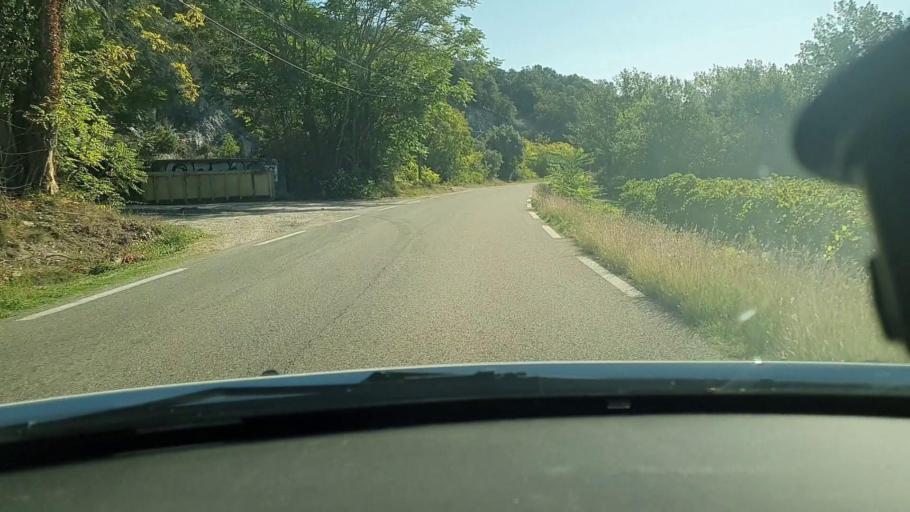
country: FR
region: Languedoc-Roussillon
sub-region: Departement du Gard
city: Saint-Julien-de-Peyrolas
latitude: 44.2985
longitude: 4.5205
